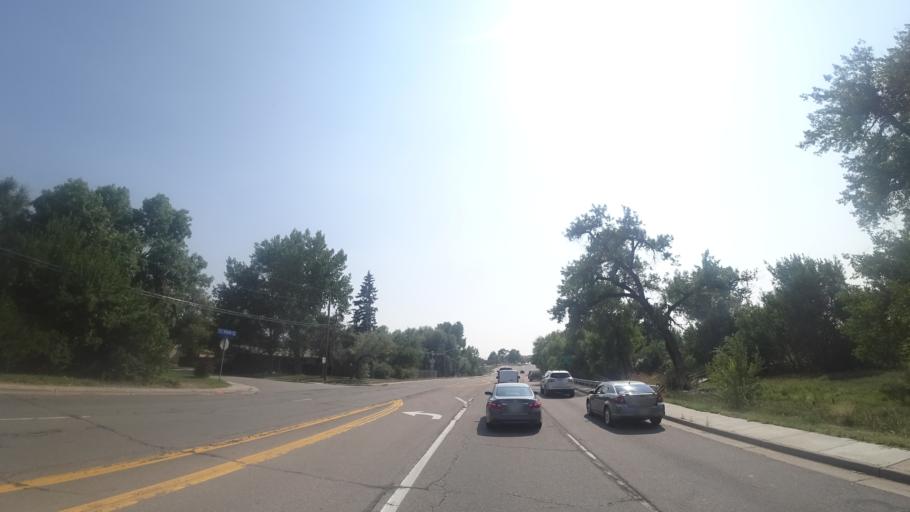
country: US
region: Colorado
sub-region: Arapahoe County
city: Southglenn
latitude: 39.5984
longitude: -104.9573
